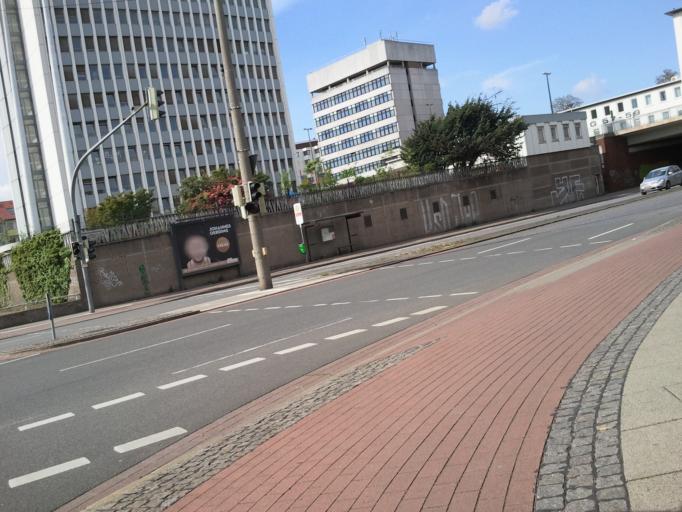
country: DE
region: Bremen
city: Bremen
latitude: 53.0846
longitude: 8.8033
